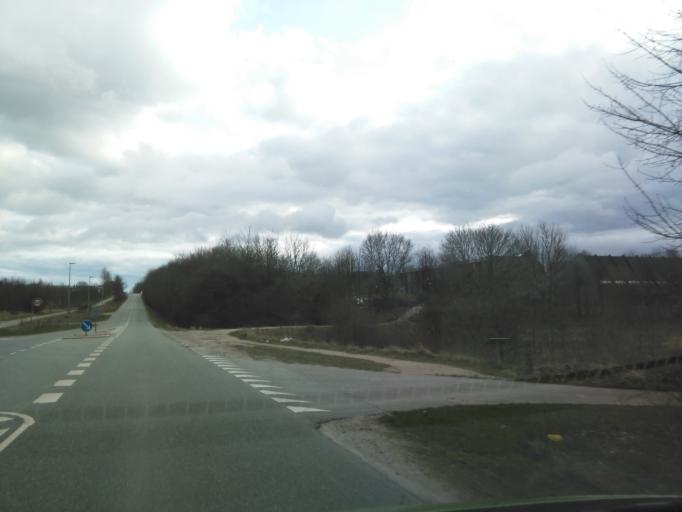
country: DK
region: Central Jutland
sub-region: Arhus Kommune
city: Stavtrup
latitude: 56.1712
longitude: 10.1192
